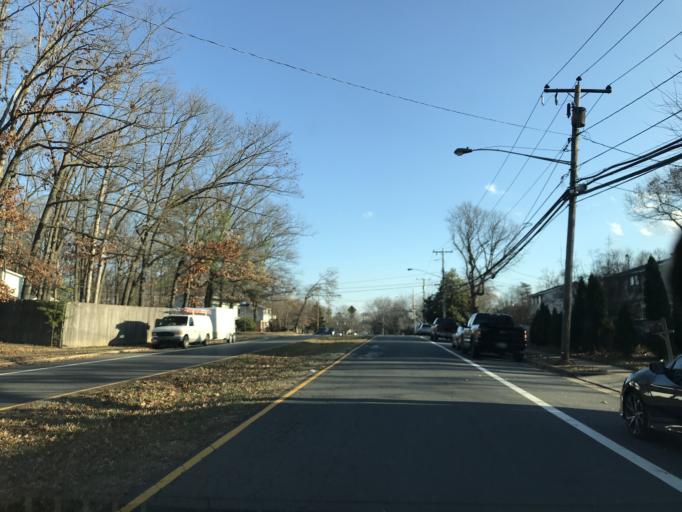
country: US
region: Virginia
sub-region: Fairfax County
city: West Springfield
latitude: 38.7682
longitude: -77.2260
